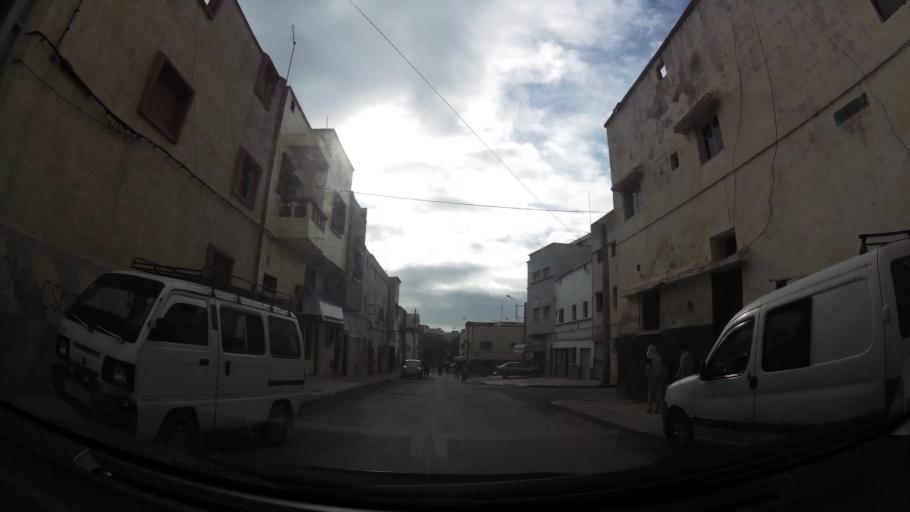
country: MA
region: Doukkala-Abda
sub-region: El-Jadida
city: El Jadida
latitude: 33.2542
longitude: -8.5169
